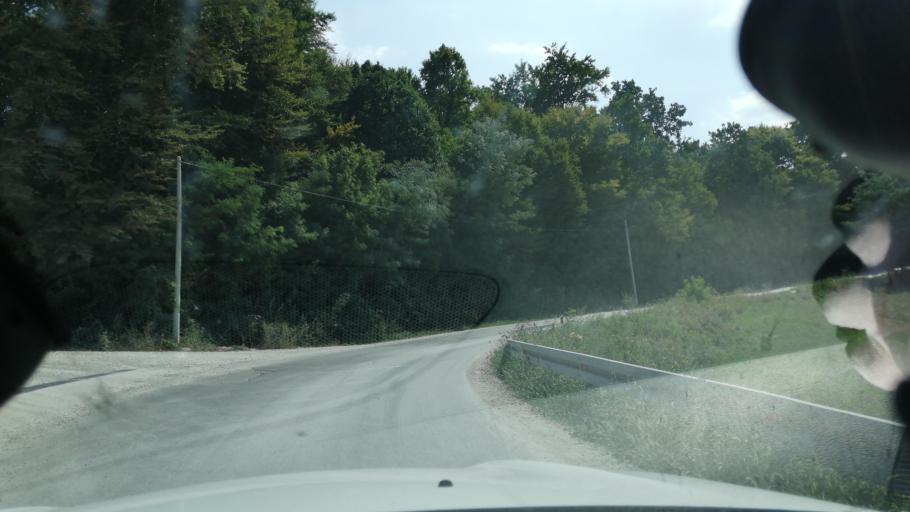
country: RS
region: Central Serbia
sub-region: Moravicki Okrug
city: Cacak
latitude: 43.8488
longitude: 20.3029
